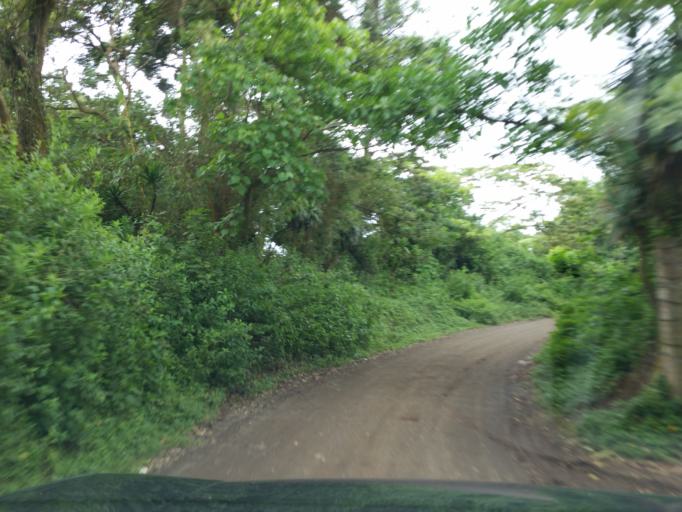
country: NI
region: Managua
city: El Crucero
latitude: 12.0120
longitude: -86.2770
